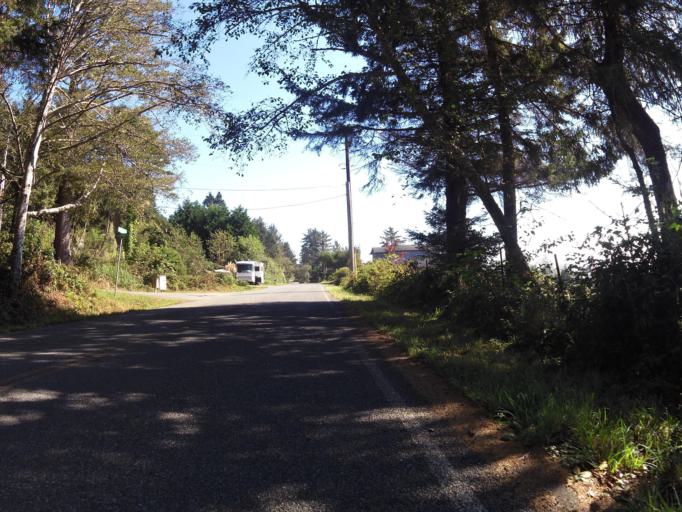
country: US
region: Oregon
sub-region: Curry County
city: Harbor
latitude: 41.9503
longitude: -124.1972
